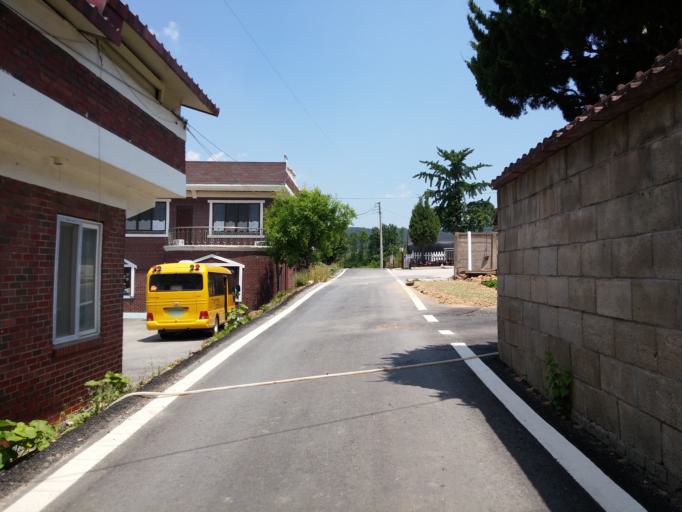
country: KR
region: Chungcheongbuk-do
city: Cheongju-si
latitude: 36.5555
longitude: 127.4360
